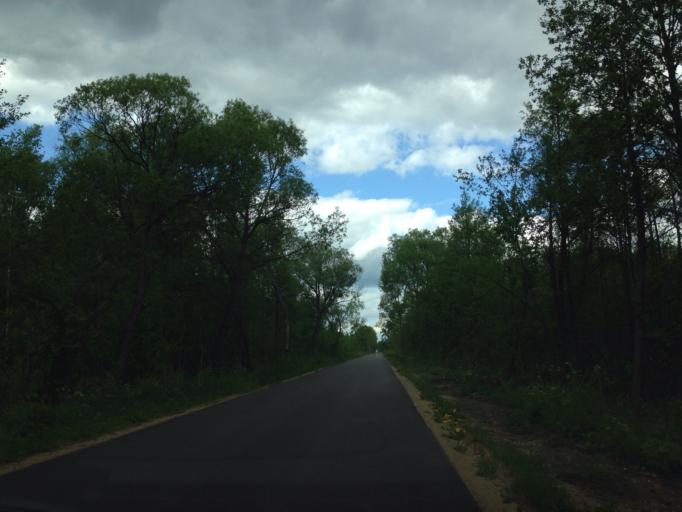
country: PL
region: Podlasie
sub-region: Powiat bialostocki
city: Tykocin
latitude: 53.3035
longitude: 22.6042
